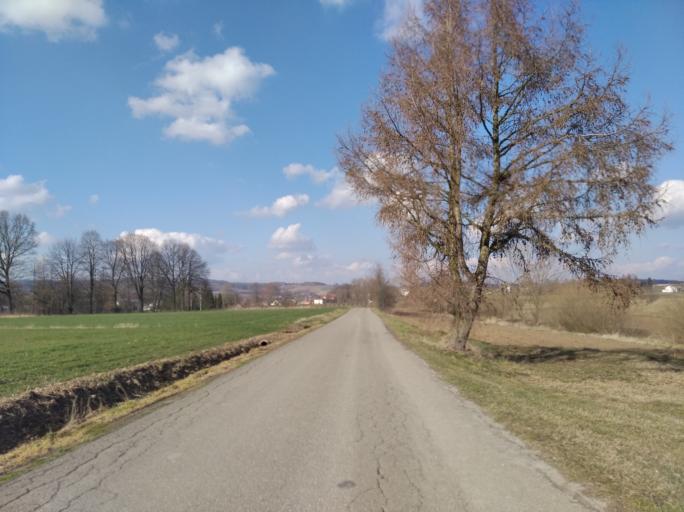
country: PL
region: Subcarpathian Voivodeship
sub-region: Powiat strzyzowski
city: Wysoka Strzyzowska
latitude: 49.8565
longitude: 21.7091
